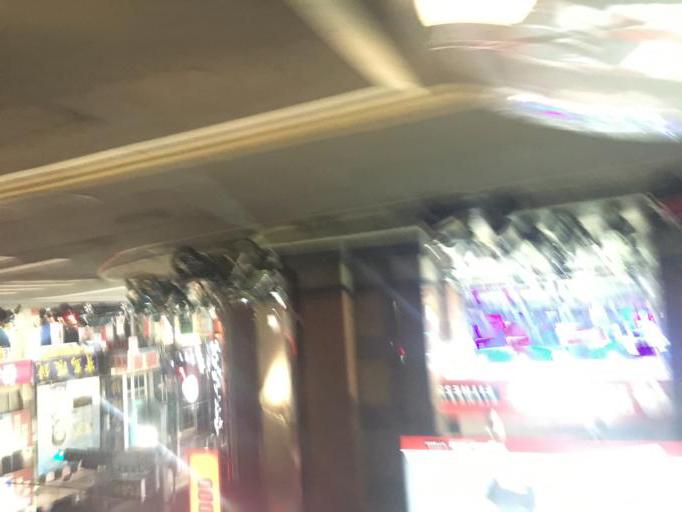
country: TW
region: Taiwan
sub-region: Hsinchu
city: Hsinchu
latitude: 24.8060
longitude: 120.9693
